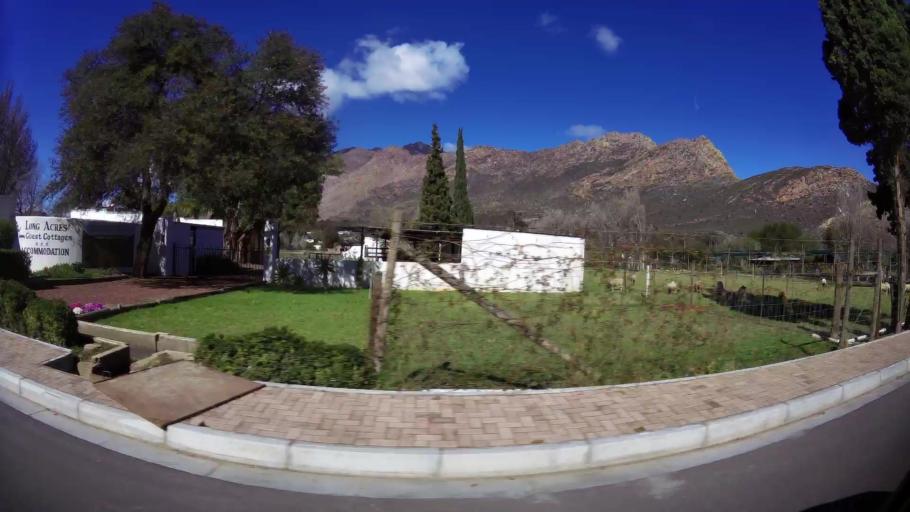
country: ZA
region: Western Cape
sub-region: Cape Winelands District Municipality
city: Ashton
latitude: -33.7901
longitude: 20.1160
